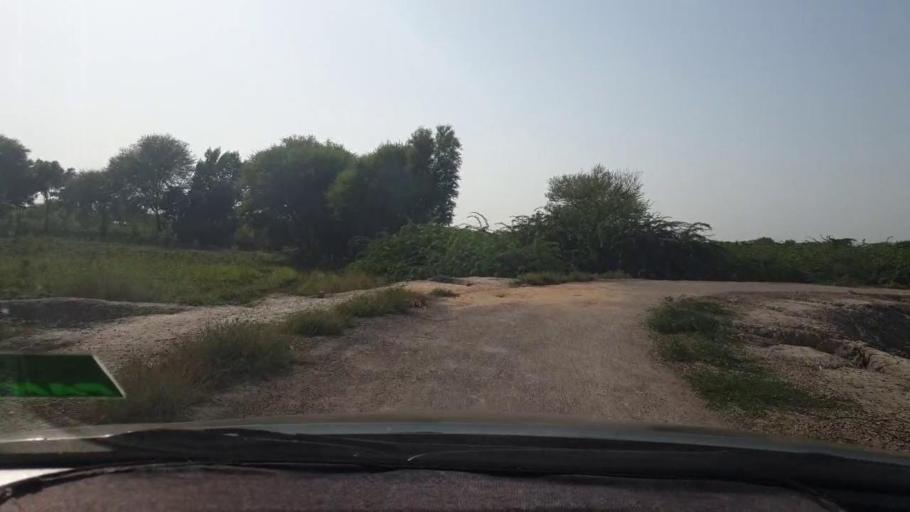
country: PK
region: Sindh
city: Naukot
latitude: 24.8695
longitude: 69.3174
